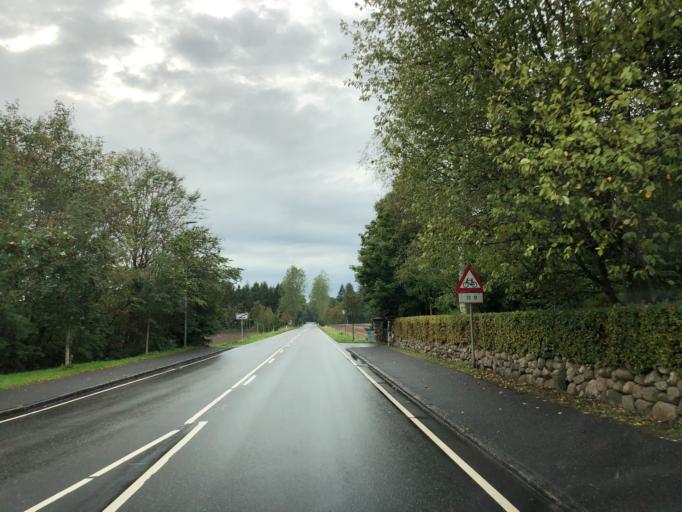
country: DK
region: Central Jutland
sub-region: Ikast-Brande Kommune
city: Brande
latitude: 56.0088
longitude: 9.1070
